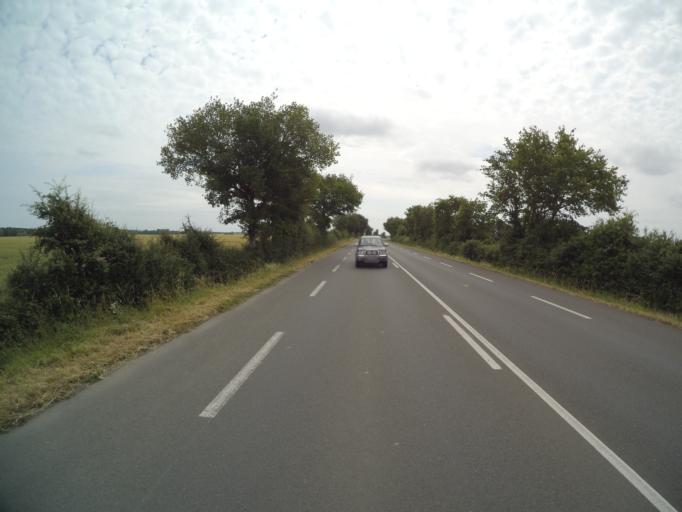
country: FR
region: Pays de la Loire
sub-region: Departement de la Vendee
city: Chavagnes-en-Paillers
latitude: 46.9217
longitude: -1.2493
